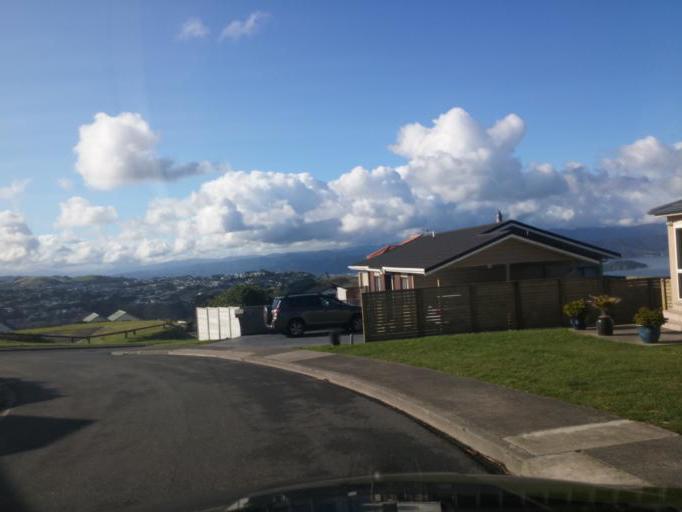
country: NZ
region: Wellington
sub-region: Wellington City
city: Wellington
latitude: -41.2361
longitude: 174.7920
